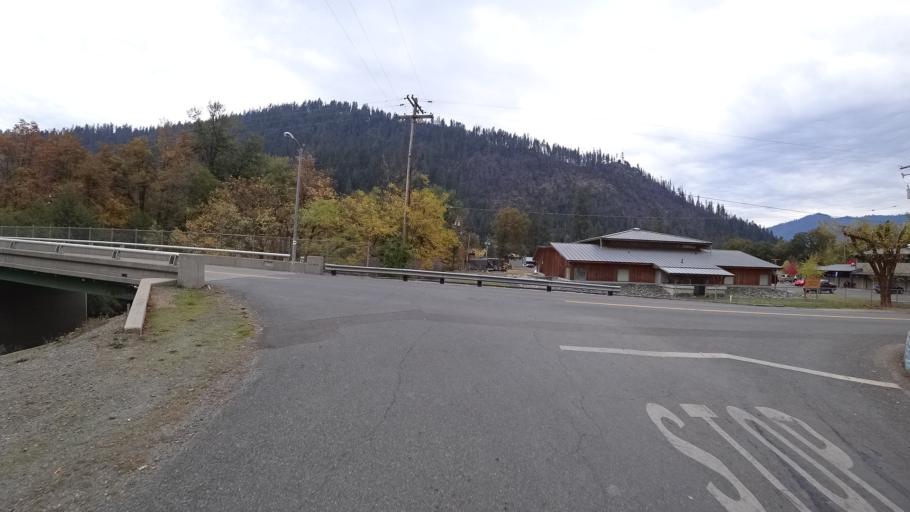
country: US
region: California
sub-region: Siskiyou County
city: Happy Camp
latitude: 41.7926
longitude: -123.3797
